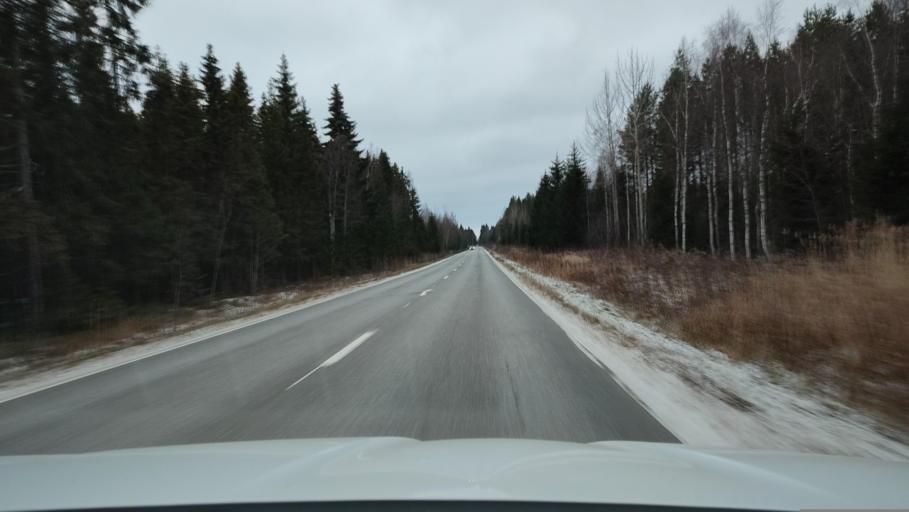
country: FI
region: Ostrobothnia
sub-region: Vaasa
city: Replot
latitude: 63.2598
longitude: 21.3634
